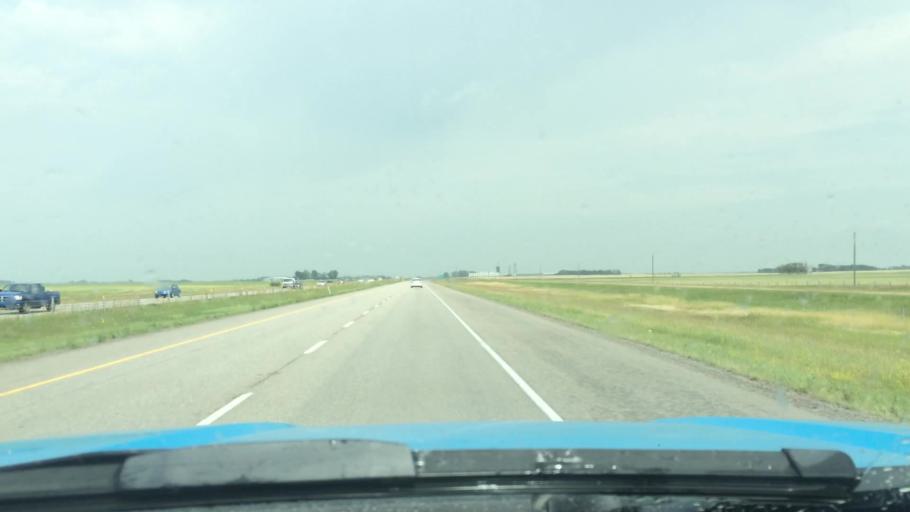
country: CA
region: Alberta
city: Olds
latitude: 51.7020
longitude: -114.0251
